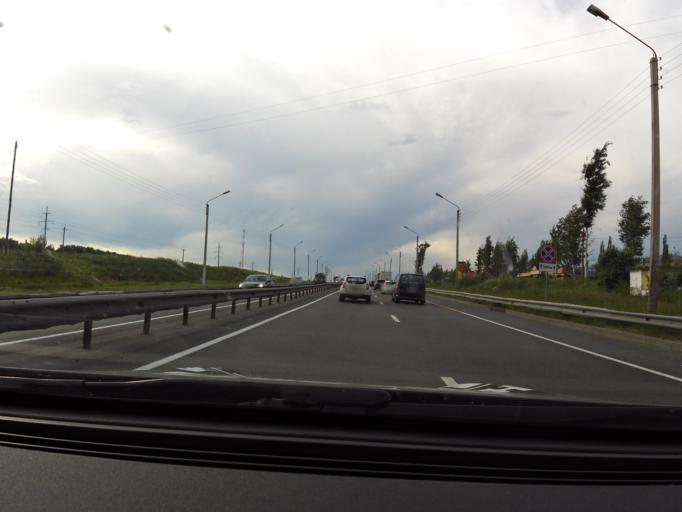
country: RU
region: Vladimir
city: Vyazniki
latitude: 56.2285
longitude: 42.1224
